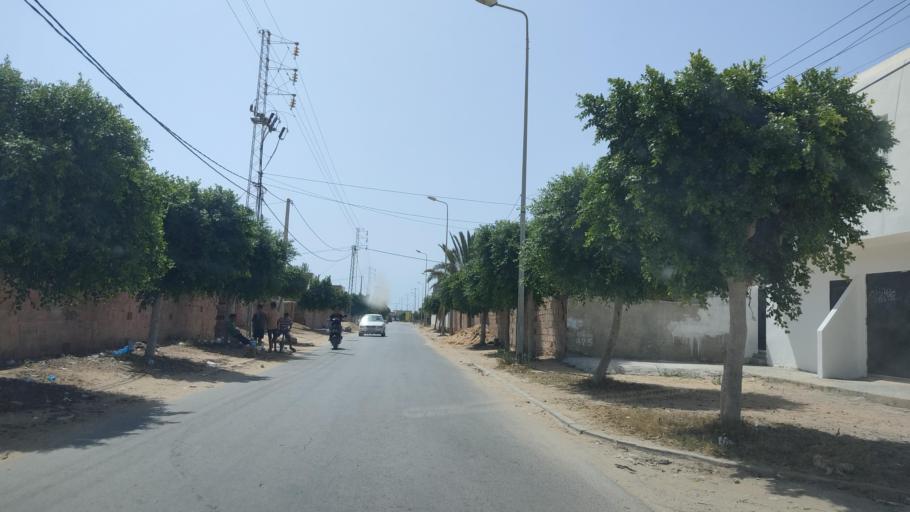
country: TN
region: Safaqis
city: Sfax
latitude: 34.6715
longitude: 10.7042
